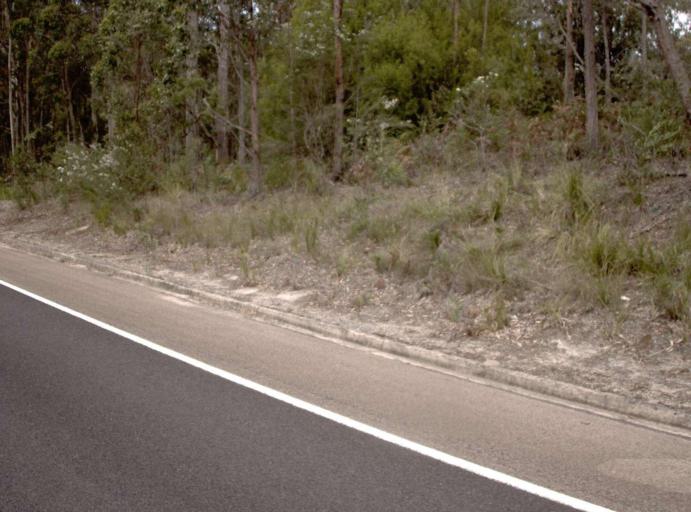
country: AU
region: New South Wales
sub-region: Bega Valley
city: Eden
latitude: -37.3994
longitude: 149.6711
